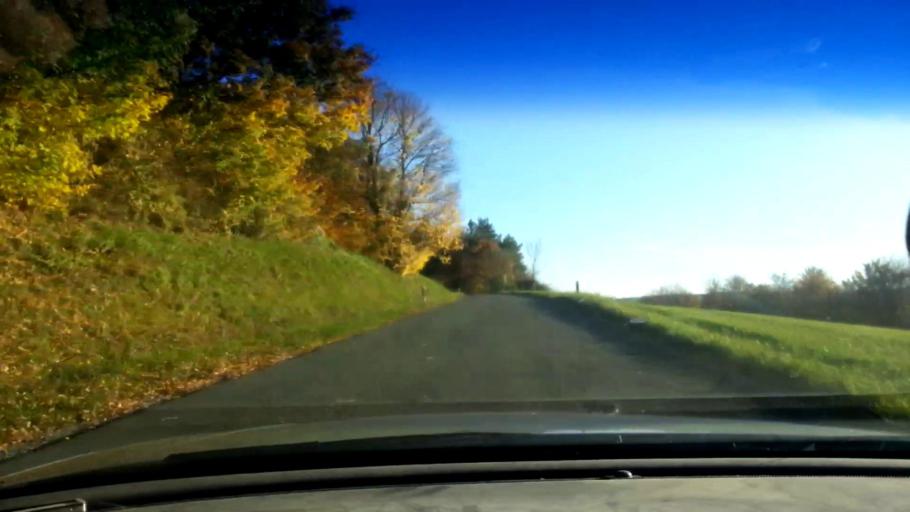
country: DE
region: Bavaria
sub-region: Upper Franconia
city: Heiligenstadt
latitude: 49.8688
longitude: 11.1779
